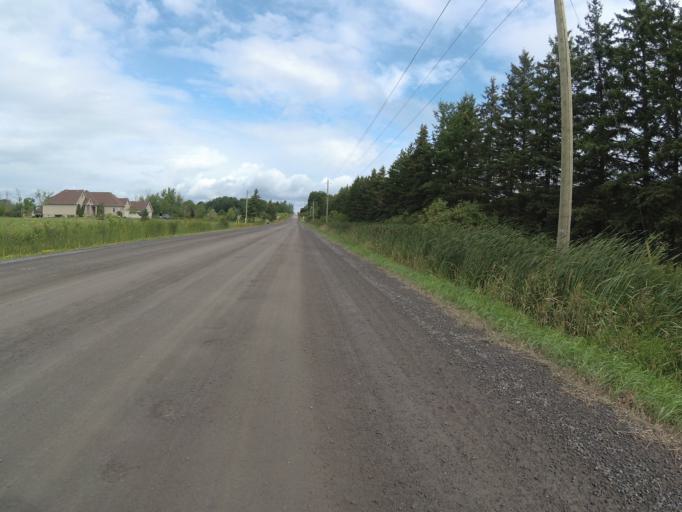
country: CA
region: Ontario
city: Clarence-Rockland
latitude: 45.4837
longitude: -75.3107
